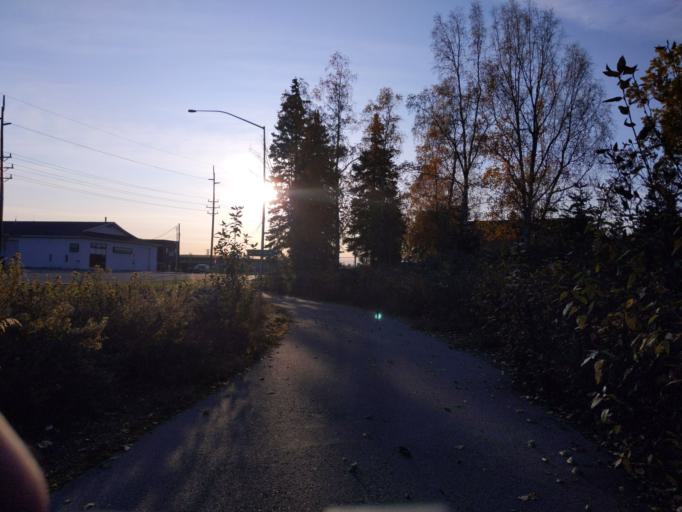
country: US
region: Alaska
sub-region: Anchorage Municipality
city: Anchorage
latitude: 61.1668
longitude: -149.8781
